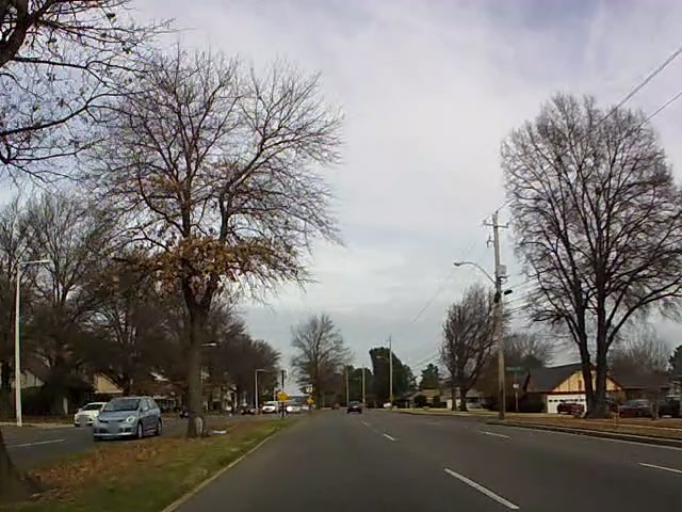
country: US
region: Tennessee
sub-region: Shelby County
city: Germantown
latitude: 35.0557
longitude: -89.8440
